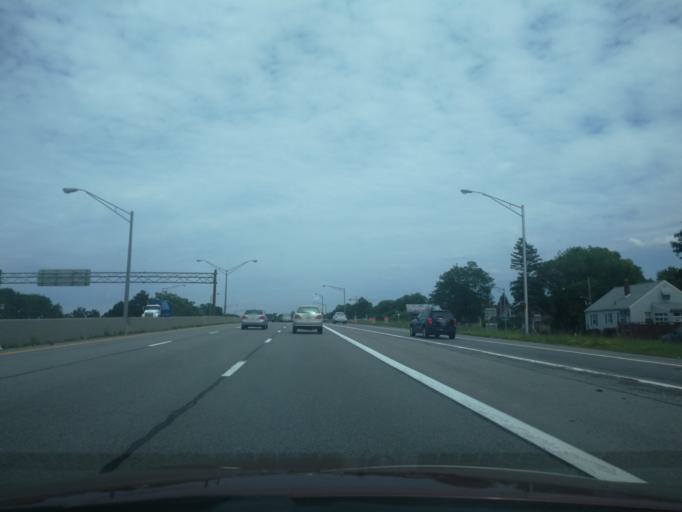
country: US
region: New York
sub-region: Monroe County
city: Irondequoit
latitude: 43.1918
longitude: -77.6022
